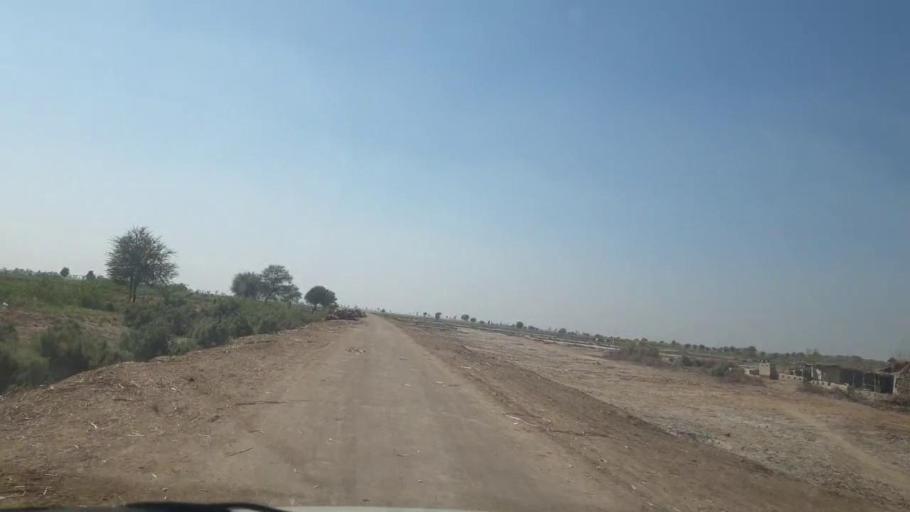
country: PK
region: Sindh
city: Mirpur Khas
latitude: 25.4707
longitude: 69.1718
